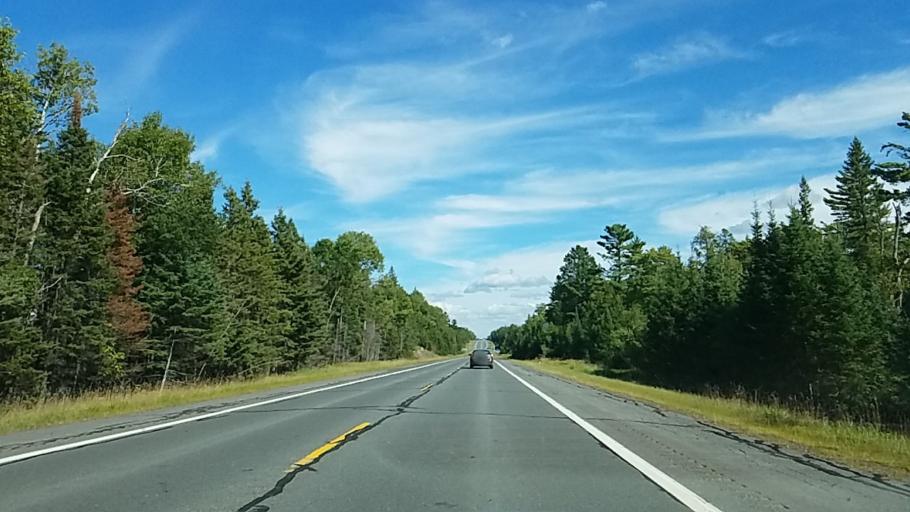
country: US
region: Michigan
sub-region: Baraga County
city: L'Anse
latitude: 46.5762
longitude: -88.3479
